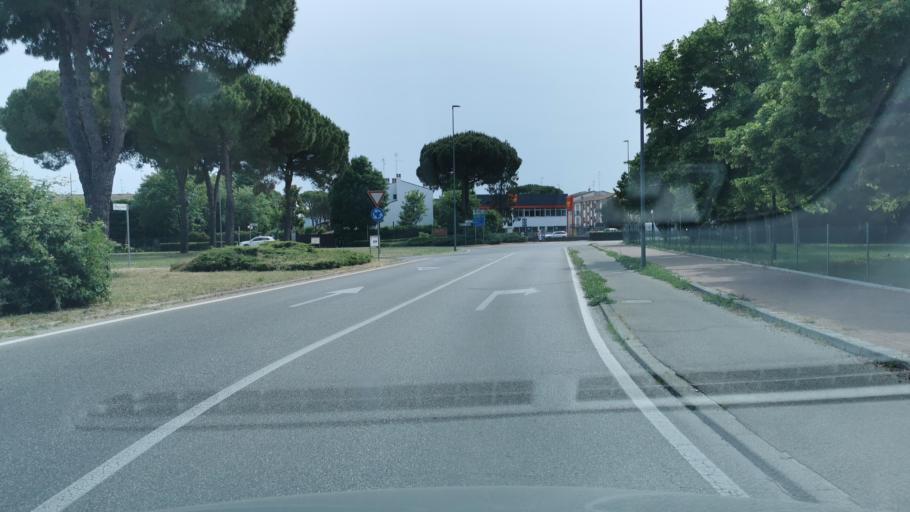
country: IT
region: Emilia-Romagna
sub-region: Provincia di Ravenna
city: Ravenna
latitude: 44.4232
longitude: 12.1820
